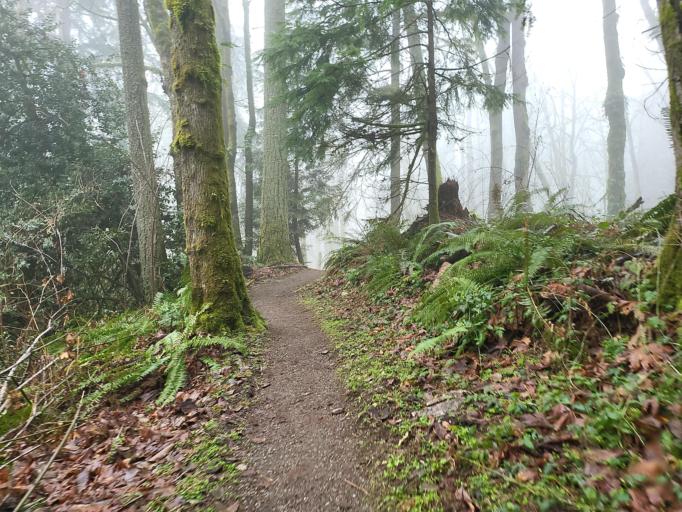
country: US
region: Washington
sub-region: King County
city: Newcastle
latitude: 47.5387
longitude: -122.1240
